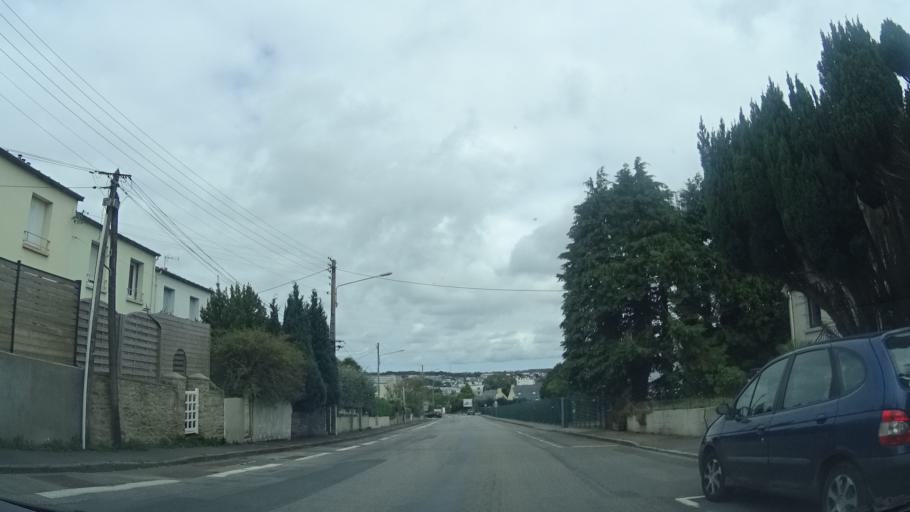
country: FR
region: Brittany
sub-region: Departement du Finistere
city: Brest
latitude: 48.4059
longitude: -4.4572
